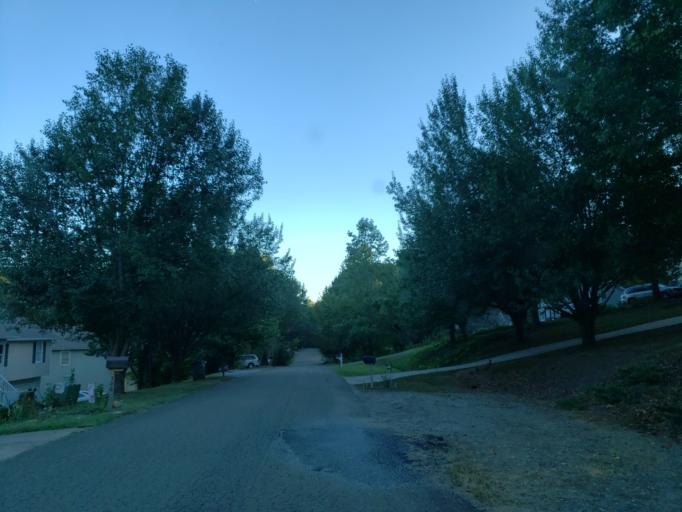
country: US
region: Georgia
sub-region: Pickens County
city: Jasper
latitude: 34.4281
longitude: -84.4350
